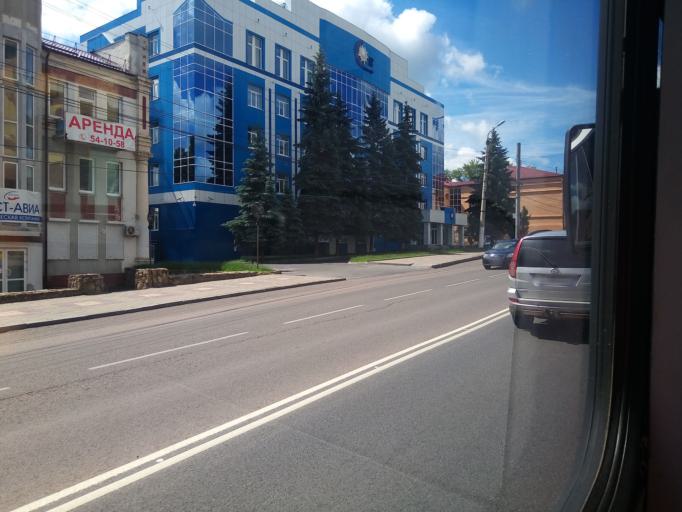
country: RU
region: Kursk
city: Kursk
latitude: 51.7250
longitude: 36.1792
